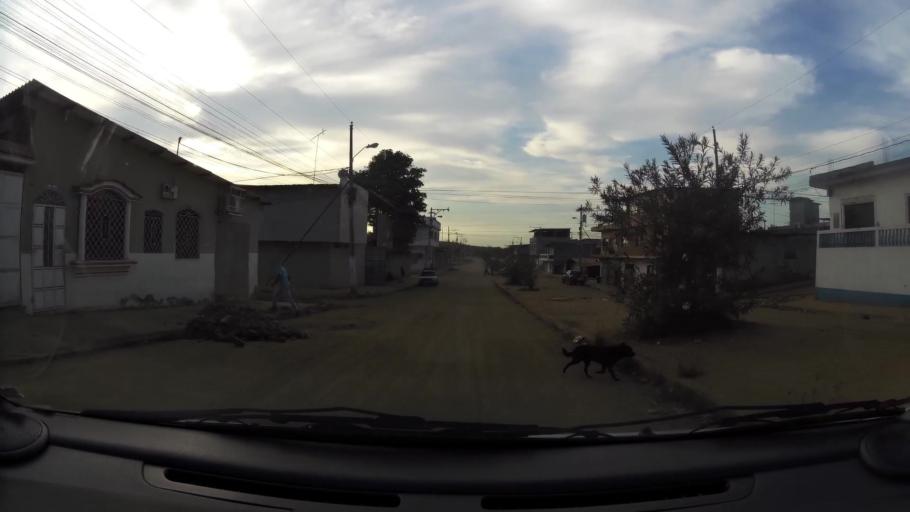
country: EC
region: Guayas
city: Eloy Alfaro
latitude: -2.0798
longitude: -79.8987
